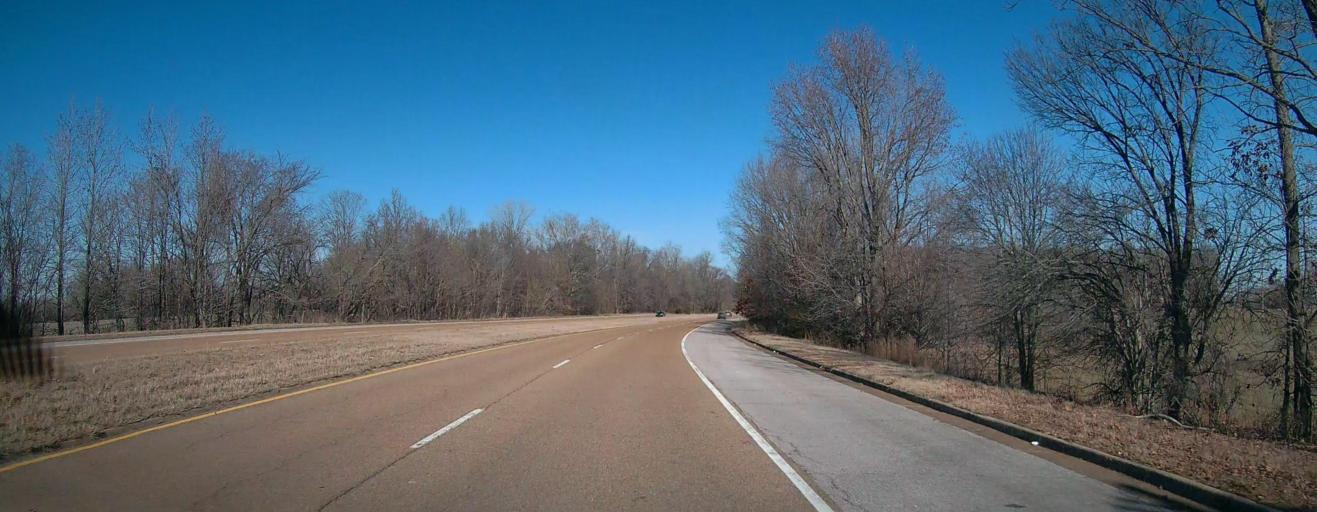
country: US
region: Tennessee
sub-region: Shelby County
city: Bartlett
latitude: 35.2531
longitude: -89.8941
